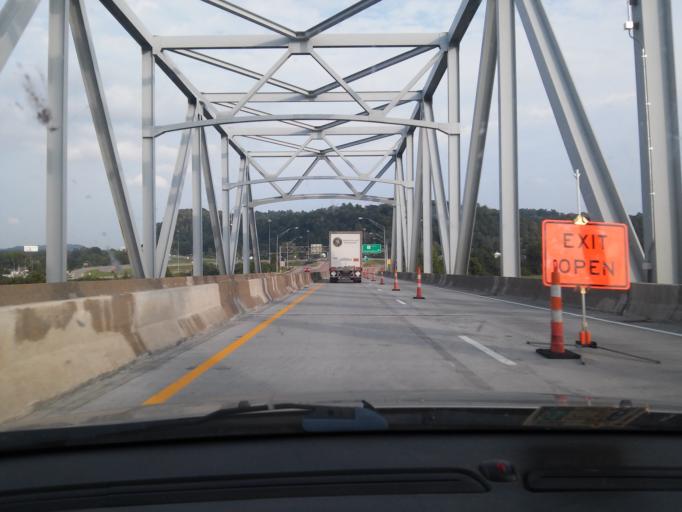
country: US
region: West Virginia
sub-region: Mason County
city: Point Pleasant
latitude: 38.8337
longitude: -82.1464
